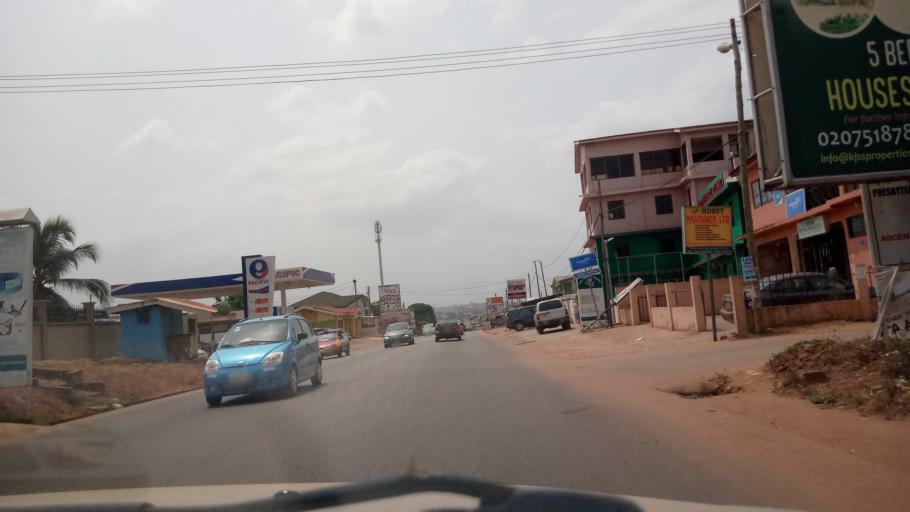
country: GH
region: Greater Accra
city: Medina Estates
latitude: 5.6832
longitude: -0.1934
